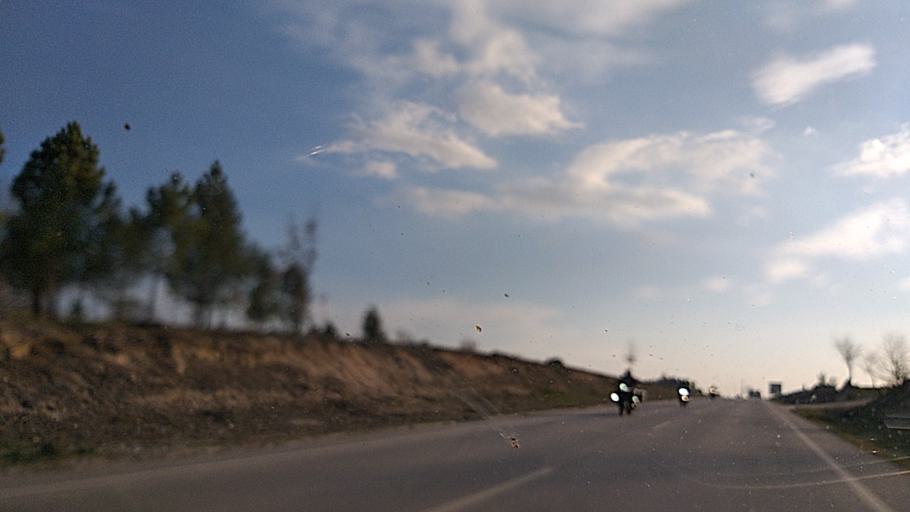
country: ES
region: Castille and Leon
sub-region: Provincia de Salamanca
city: Fuentes de Onoro
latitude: 40.6004
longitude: -6.9890
